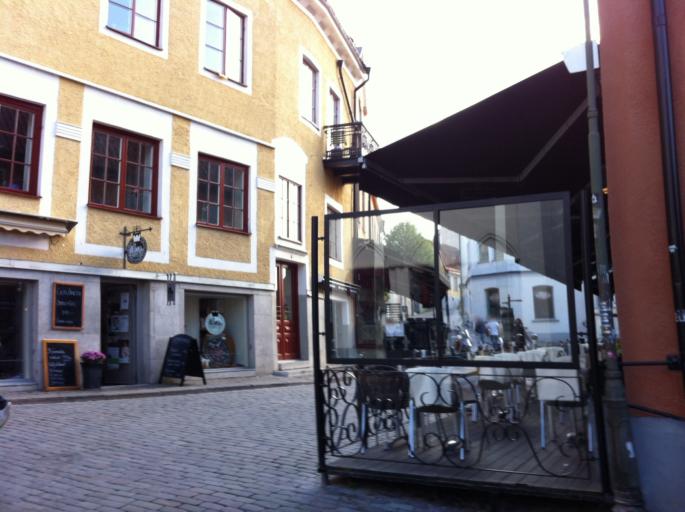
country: SE
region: Gotland
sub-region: Gotland
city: Visby
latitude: 57.6390
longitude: 18.2960
